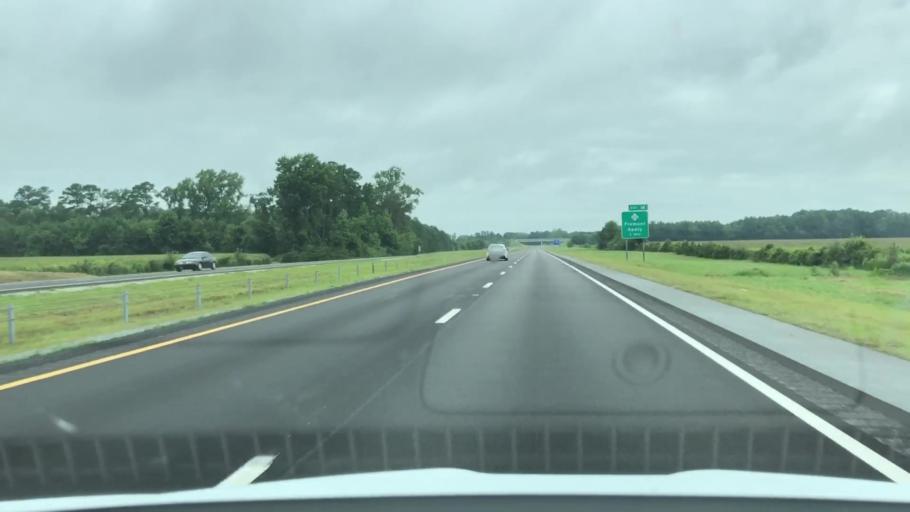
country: US
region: North Carolina
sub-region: Wayne County
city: Fremont
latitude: 35.5305
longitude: -77.9890
